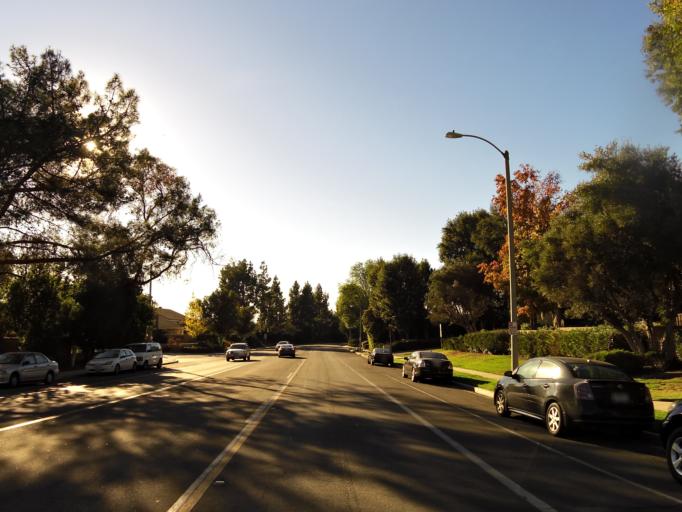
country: US
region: California
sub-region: Ventura County
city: Thousand Oaks
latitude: 34.2182
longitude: -118.8785
